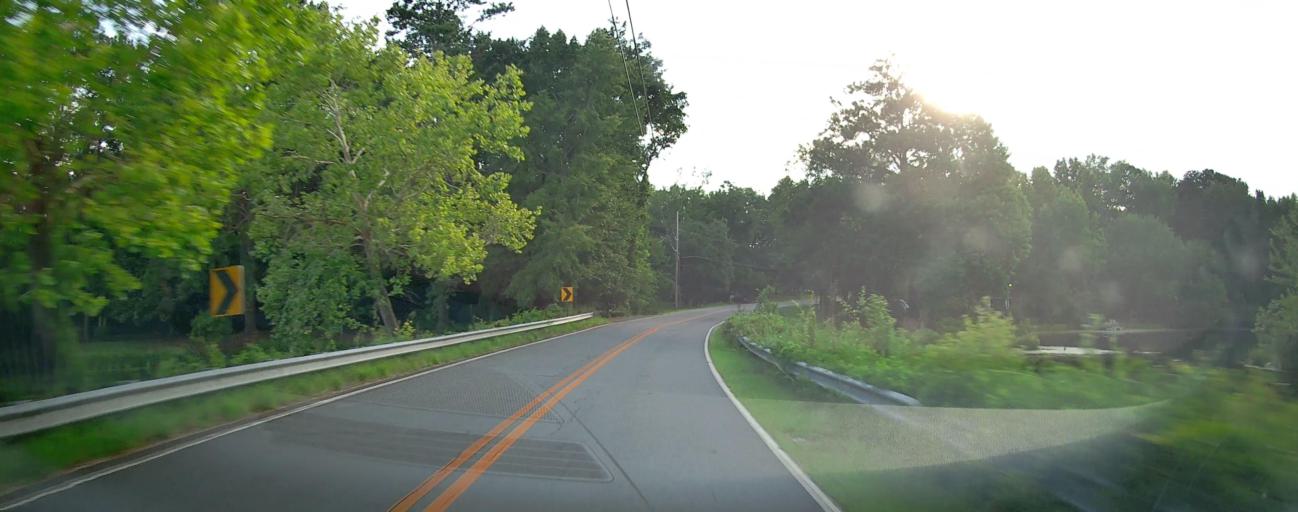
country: US
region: Georgia
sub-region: Peach County
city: Byron
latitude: 32.7166
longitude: -83.7514
